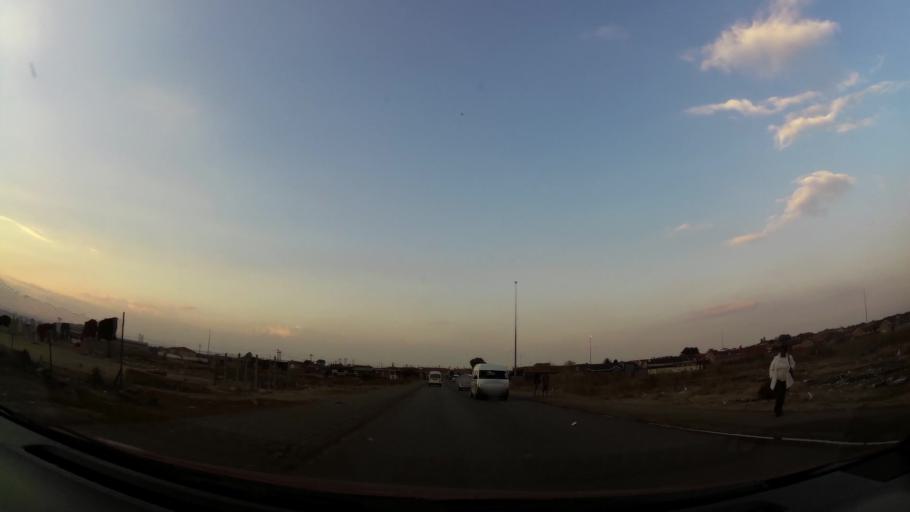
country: ZA
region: Gauteng
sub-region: City of Johannesburg Metropolitan Municipality
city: Orange Farm
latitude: -26.5639
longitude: 27.8512
